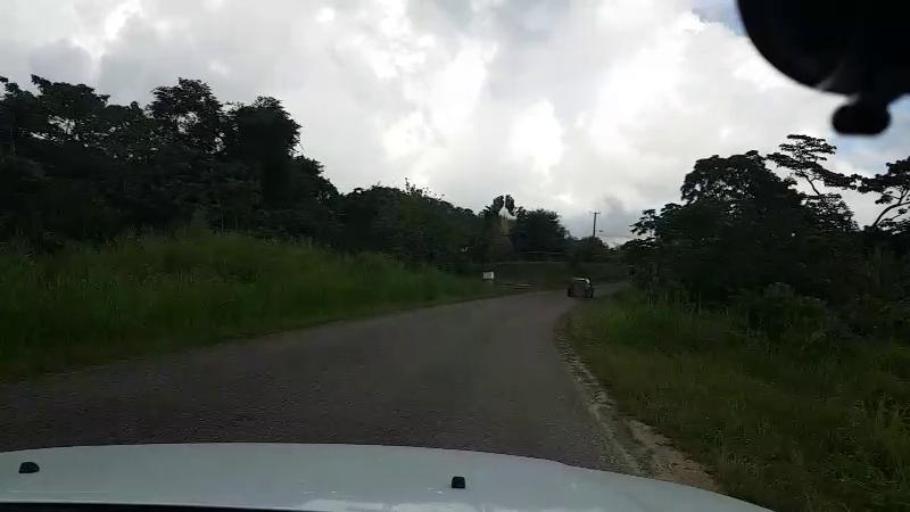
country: BZ
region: Stann Creek
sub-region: Dangriga
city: Dangriga
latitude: 17.0047
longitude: -88.4371
